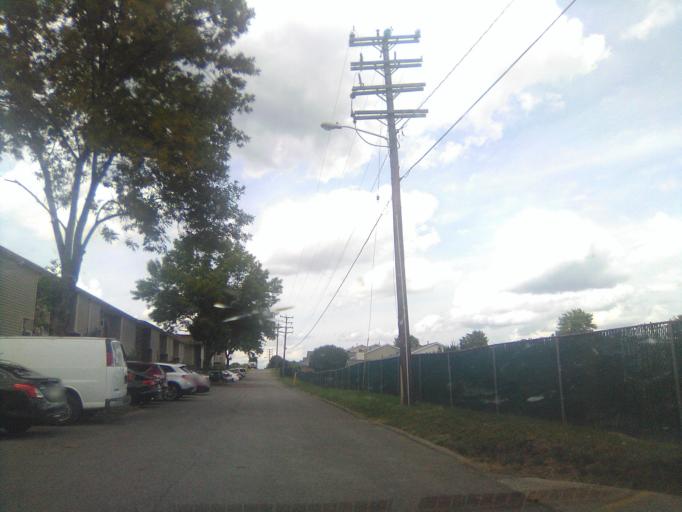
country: US
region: Tennessee
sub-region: Davidson County
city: Belle Meade
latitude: 36.0870
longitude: -86.8910
